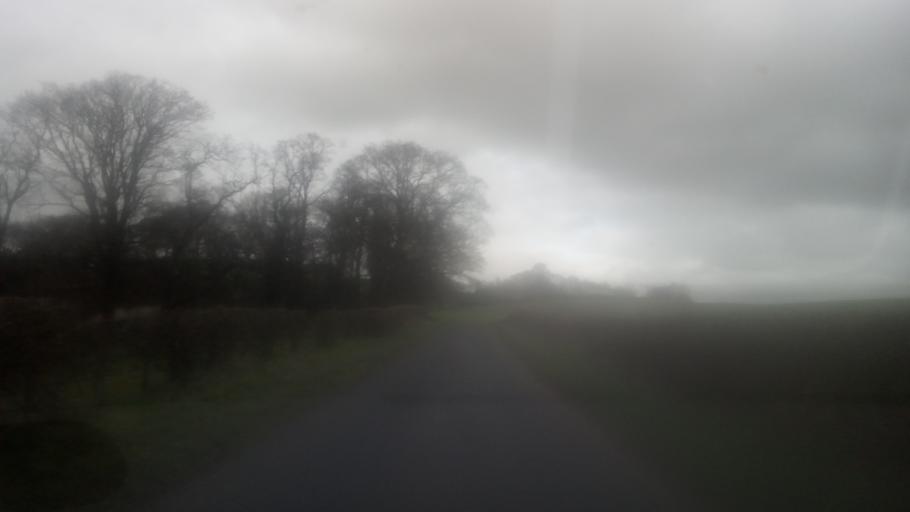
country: GB
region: Scotland
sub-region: The Scottish Borders
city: Jedburgh
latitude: 55.4874
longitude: -2.4815
